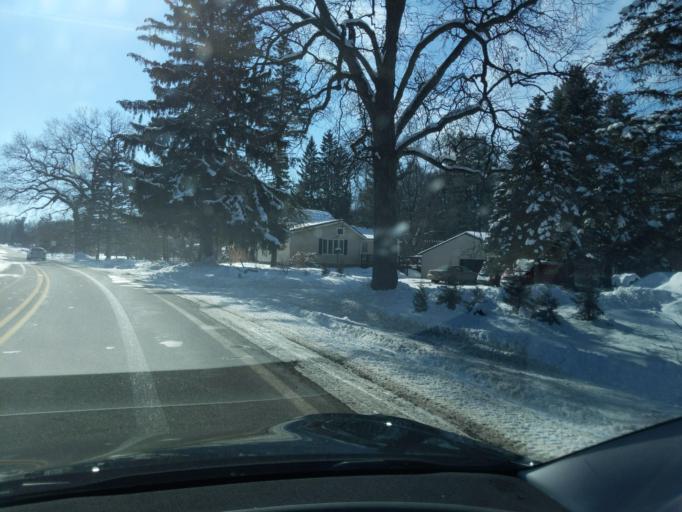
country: US
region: Michigan
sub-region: Ingham County
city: Stockbridge
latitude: 42.5240
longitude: -84.0696
